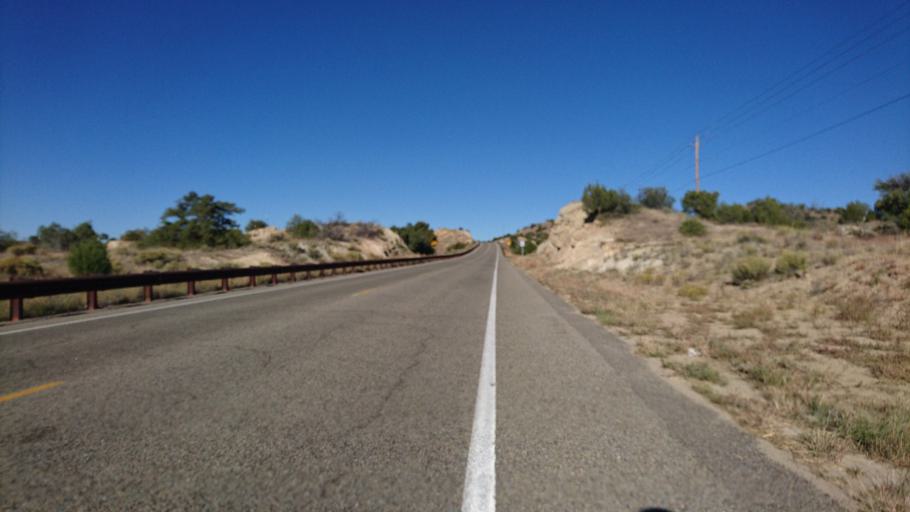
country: US
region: New Mexico
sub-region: Santa Fe County
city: La Cienega
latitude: 35.4329
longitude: -106.1022
